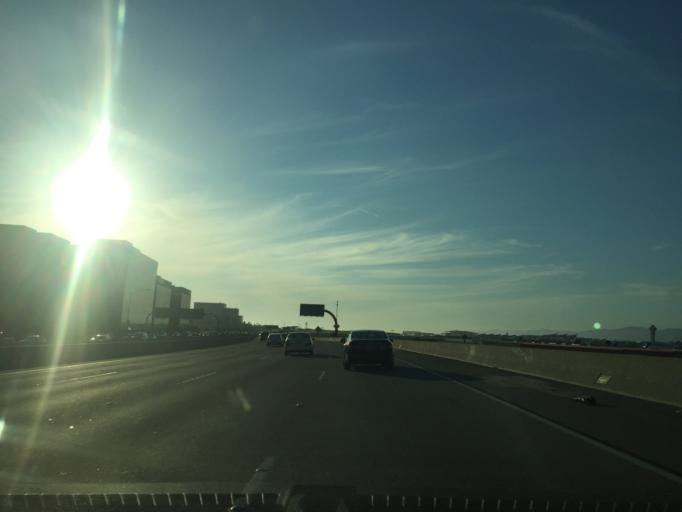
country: US
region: California
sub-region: Los Angeles County
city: Del Aire
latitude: 33.9313
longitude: -118.3807
